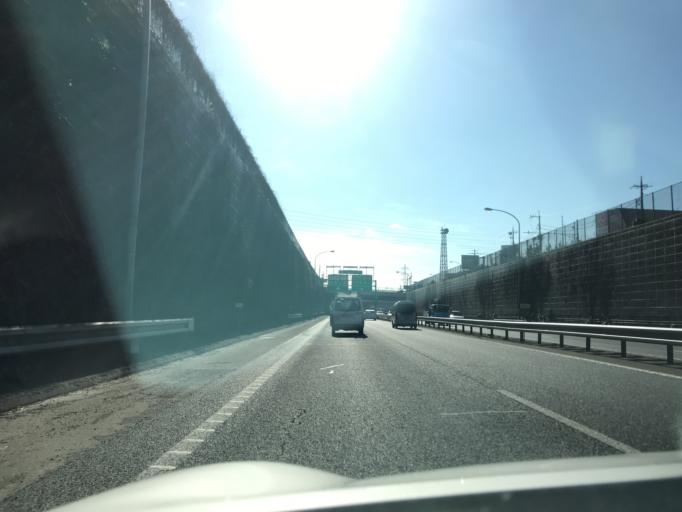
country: JP
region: Chiba
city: Chiba
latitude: 35.6165
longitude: 140.1505
